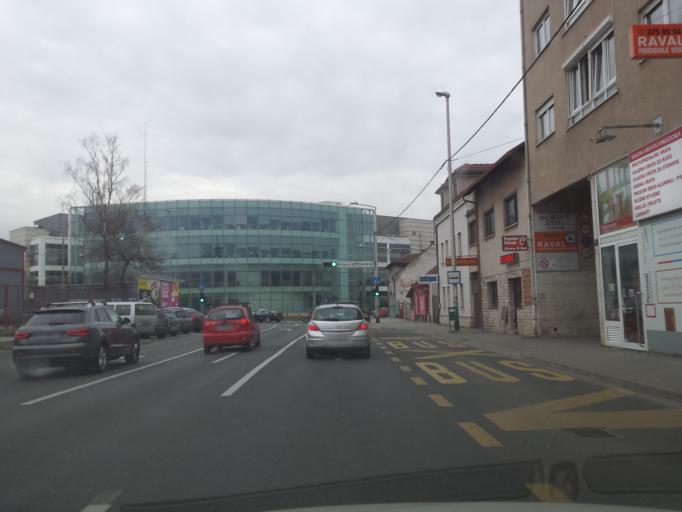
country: HR
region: Grad Zagreb
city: Jankomir
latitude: 45.8128
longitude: 15.9314
